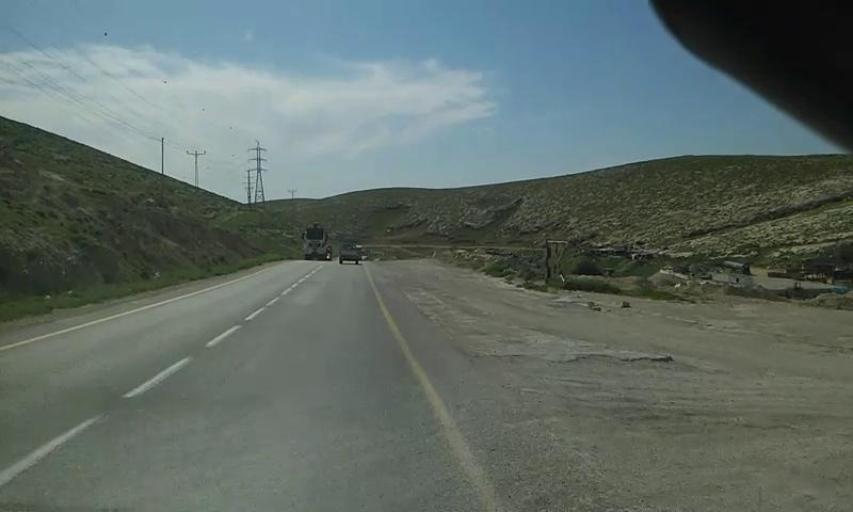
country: PS
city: Az Za`ayyim
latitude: 31.8099
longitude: 35.3065
